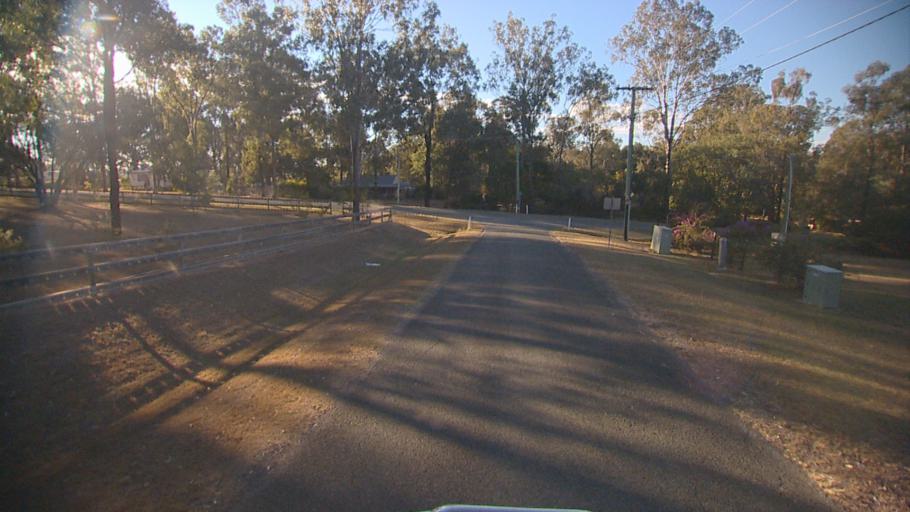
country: AU
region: Queensland
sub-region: Logan
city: Cedar Vale
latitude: -27.8638
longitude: 152.9745
